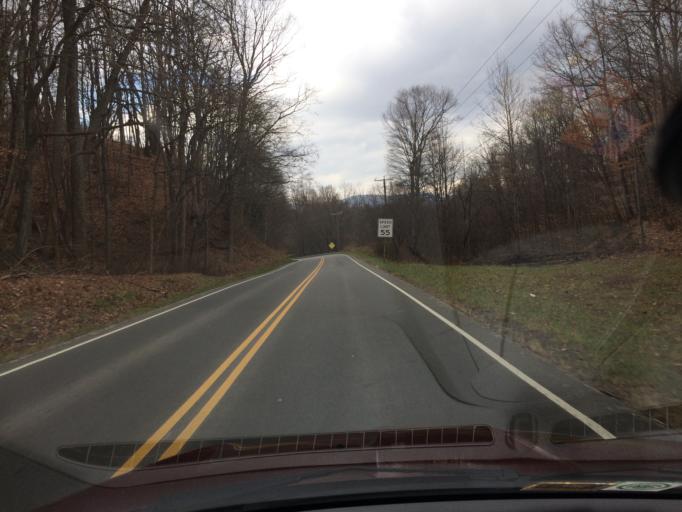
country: US
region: Virginia
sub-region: Patrick County
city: Stuart
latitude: 36.7330
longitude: -80.2462
